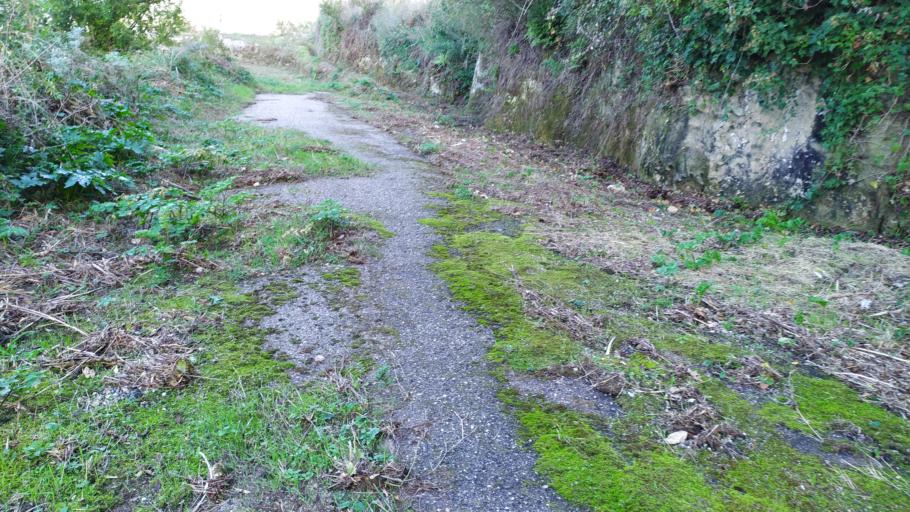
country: IT
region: Sicily
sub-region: Messina
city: Rometta
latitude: 38.1742
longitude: 15.4168
